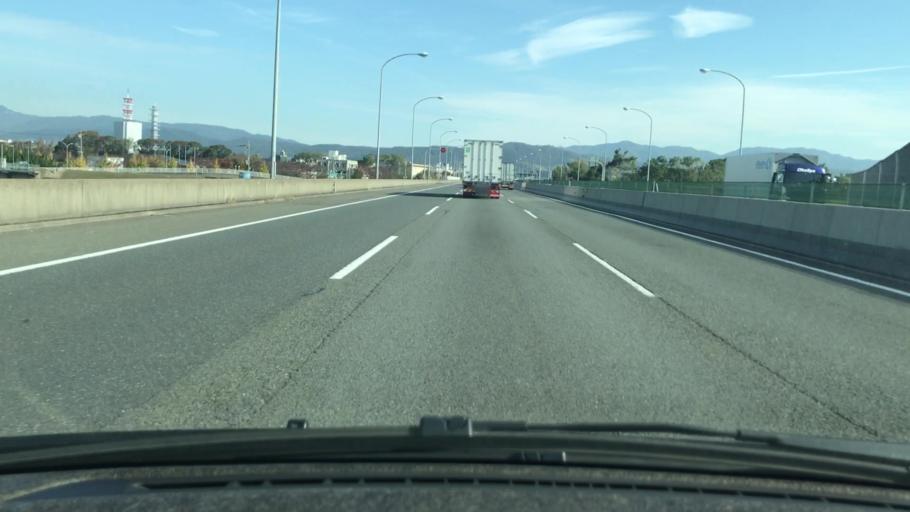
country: JP
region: Kyoto
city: Muko
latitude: 34.9497
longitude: 135.7341
